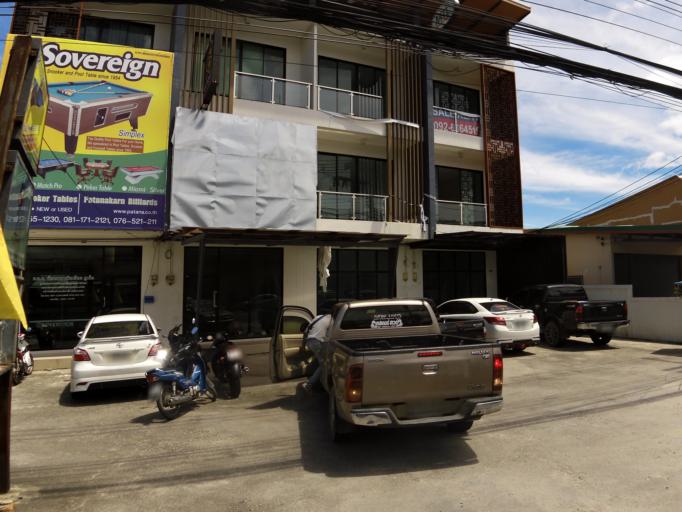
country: TH
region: Phuket
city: Ban Chalong
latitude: 7.8540
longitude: 98.3371
